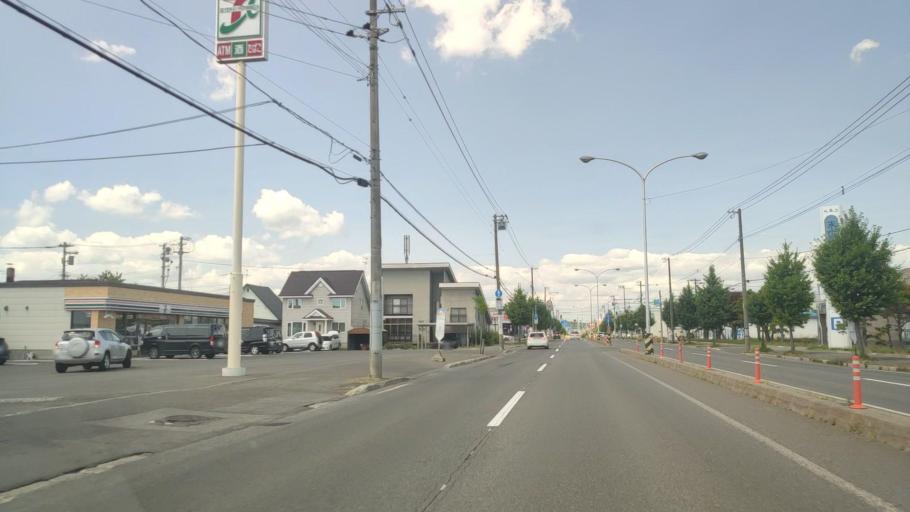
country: JP
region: Hokkaido
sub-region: Asahikawa-shi
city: Asahikawa
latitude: 43.8003
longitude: 142.3929
